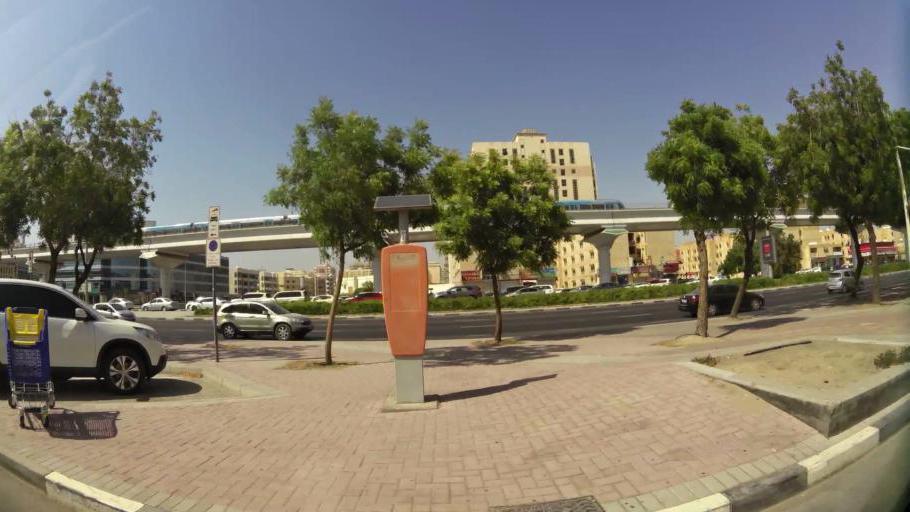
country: AE
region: Ash Shariqah
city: Sharjah
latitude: 25.2711
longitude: 55.3719
